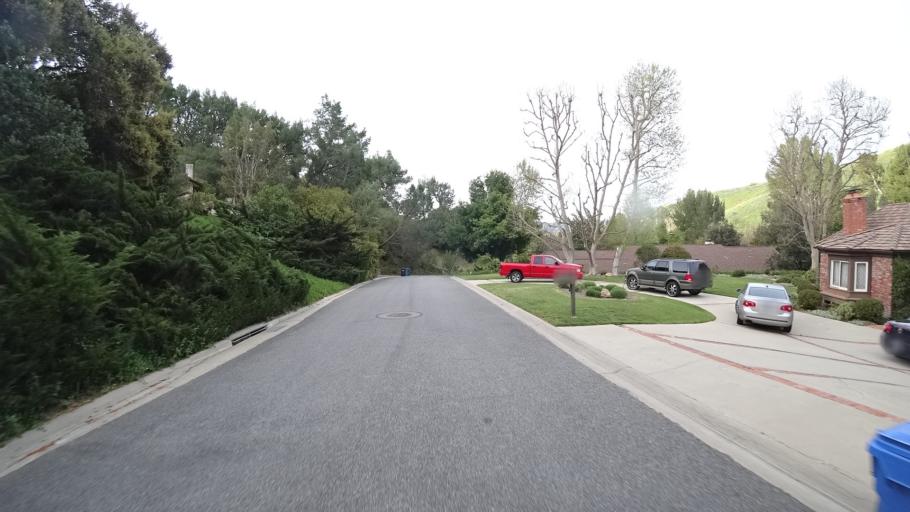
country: US
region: California
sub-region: Ventura County
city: Thousand Oaks
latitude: 34.1765
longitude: -118.8196
